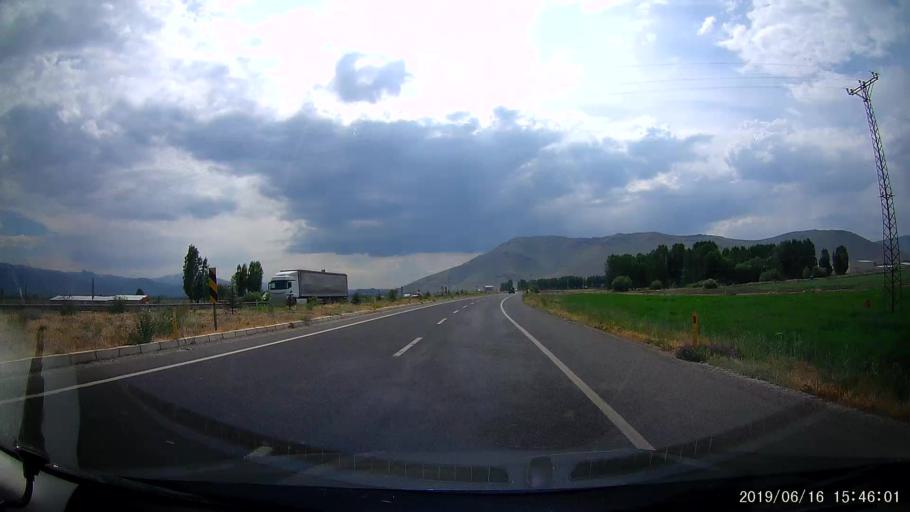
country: TR
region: Erzurum
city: Pasinler
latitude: 39.9898
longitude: 41.7536
